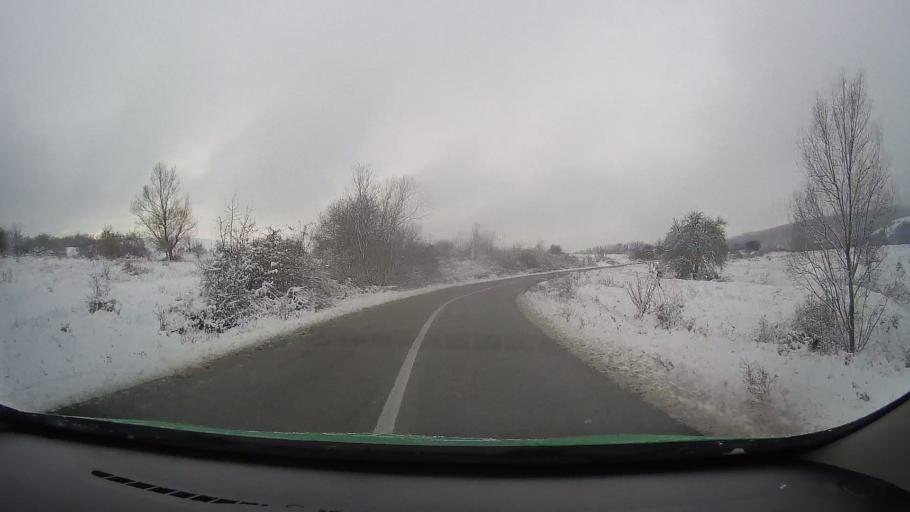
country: RO
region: Hunedoara
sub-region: Oras Hateg
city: Hateg
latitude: 45.6434
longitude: 22.9214
